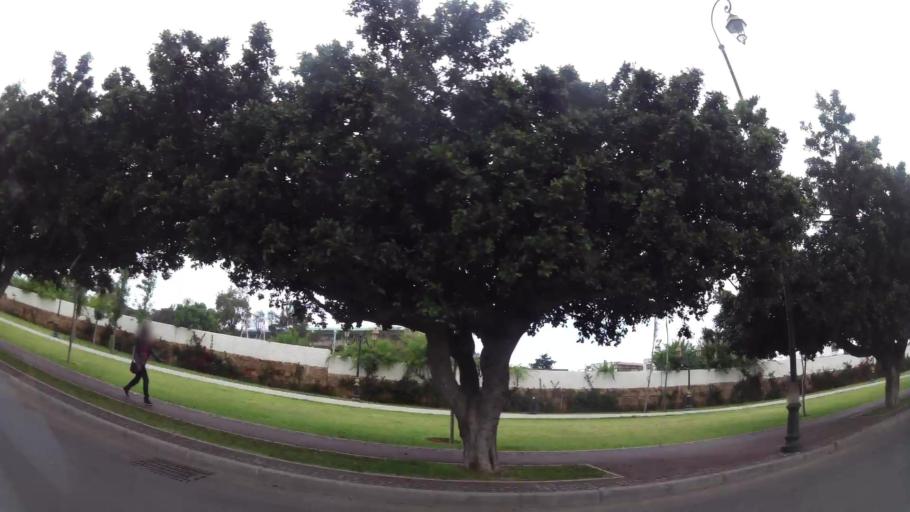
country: MA
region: Rabat-Sale-Zemmour-Zaer
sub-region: Rabat
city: Rabat
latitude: 33.9938
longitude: -6.8645
